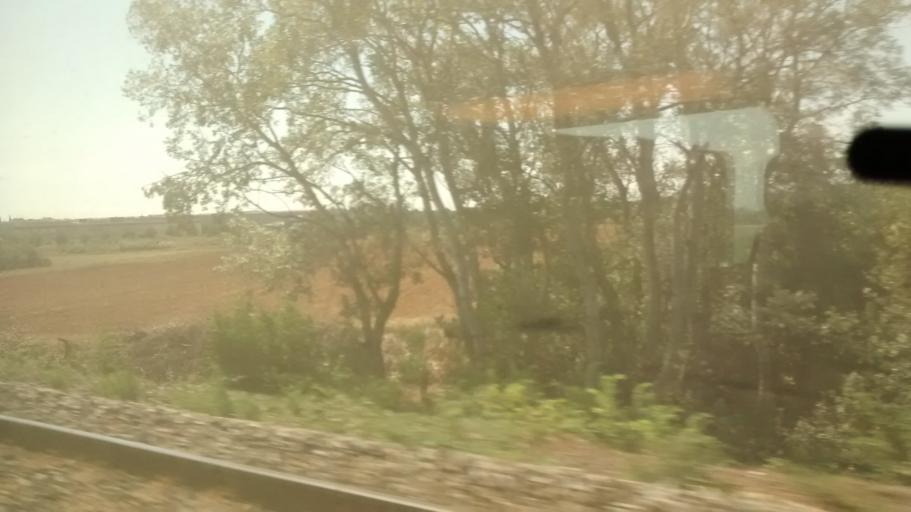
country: FR
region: Languedoc-Roussillon
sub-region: Departement de l'Herault
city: Lunel
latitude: 43.6918
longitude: 4.1493
